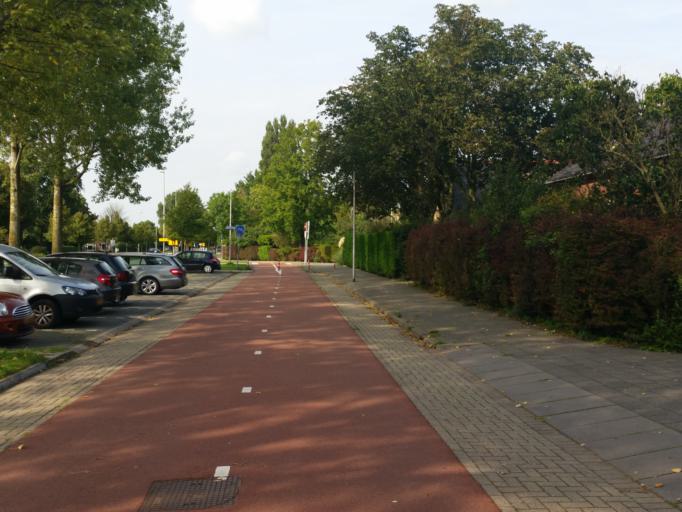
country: NL
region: South Holland
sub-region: Gemeente Pijnacker-Nootdorp
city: Pijnacker
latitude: 52.0169
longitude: 4.4294
